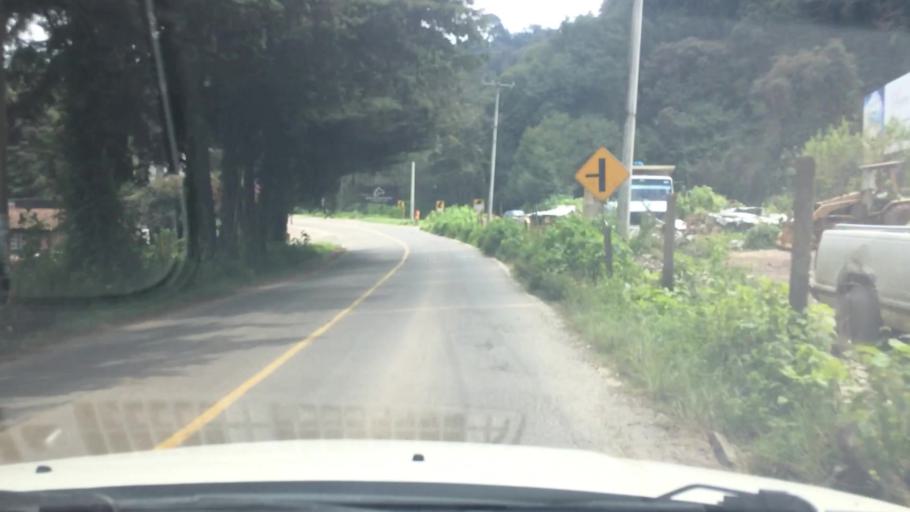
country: MX
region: Mexico
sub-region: Valle de Bravo
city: Cuadrilla de Dolores
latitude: 19.1494
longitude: -100.0559
